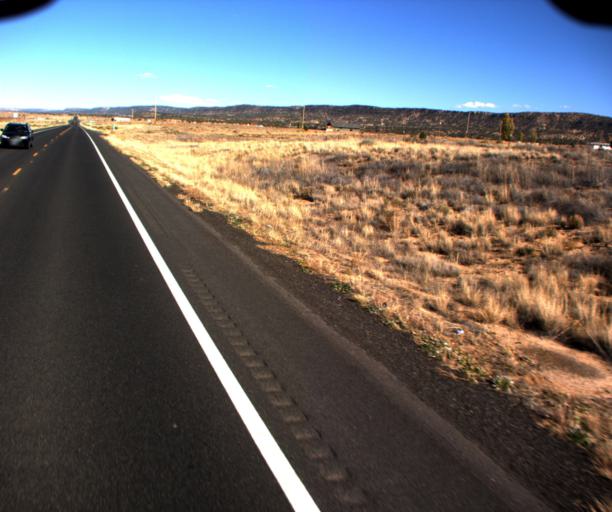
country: US
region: Arizona
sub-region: Coconino County
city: Kaibito
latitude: 36.4564
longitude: -110.7033
